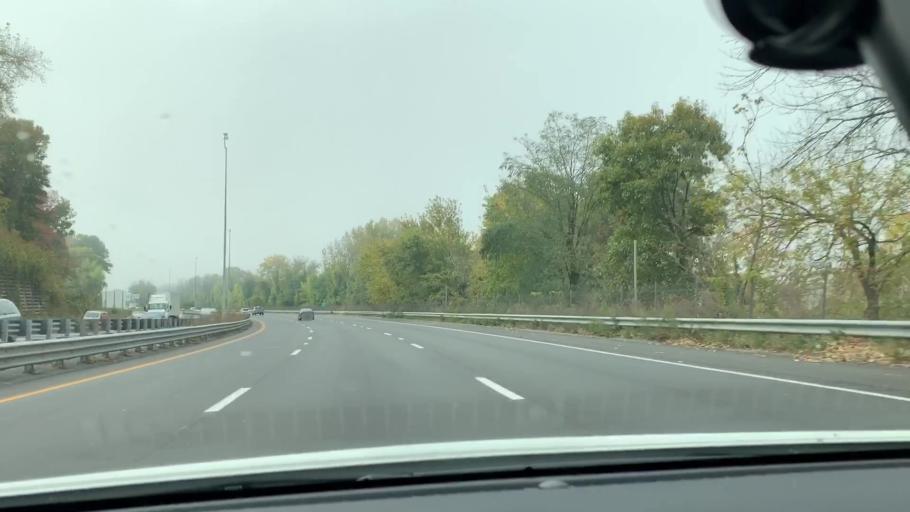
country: US
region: Massachusetts
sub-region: Hampden County
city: Longmeadow
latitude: 42.0723
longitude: -72.5871
